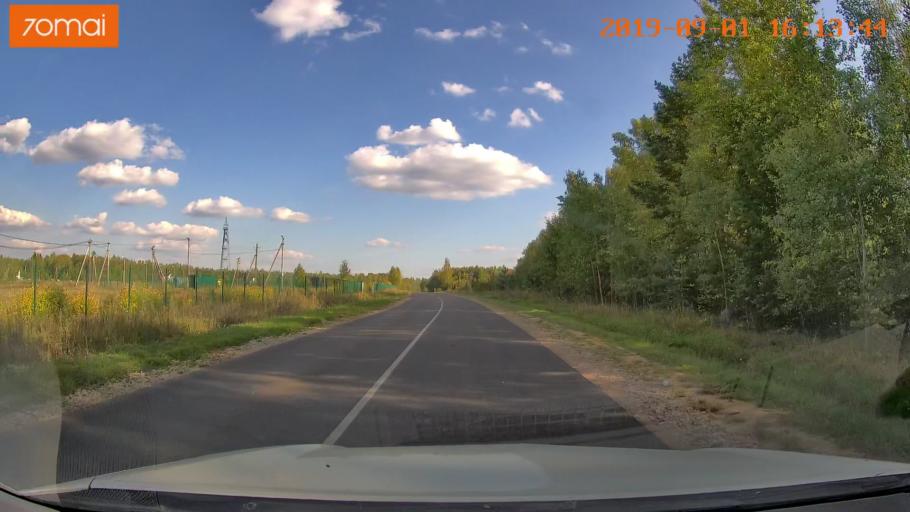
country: RU
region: Kaluga
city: Maloyaroslavets
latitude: 54.9388
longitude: 36.4615
